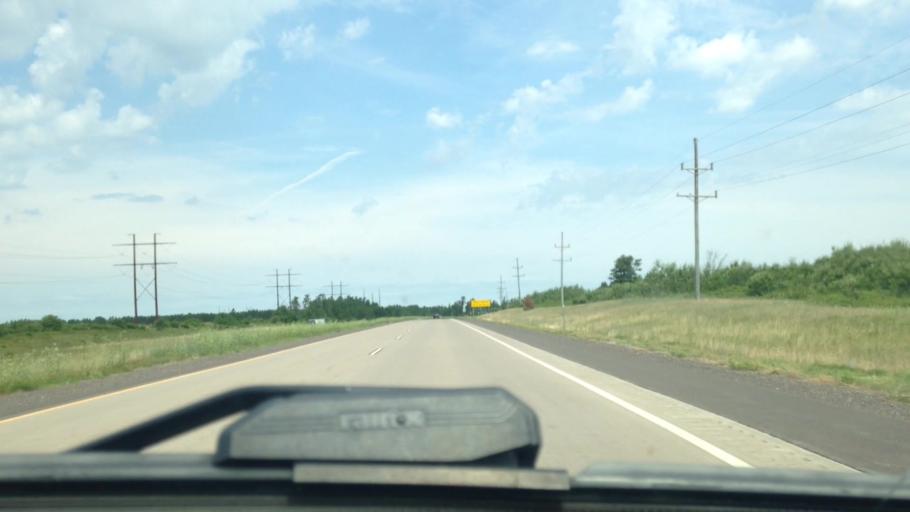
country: US
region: Wisconsin
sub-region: Douglas County
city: Lake Nebagamon
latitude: 46.2819
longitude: -91.8092
